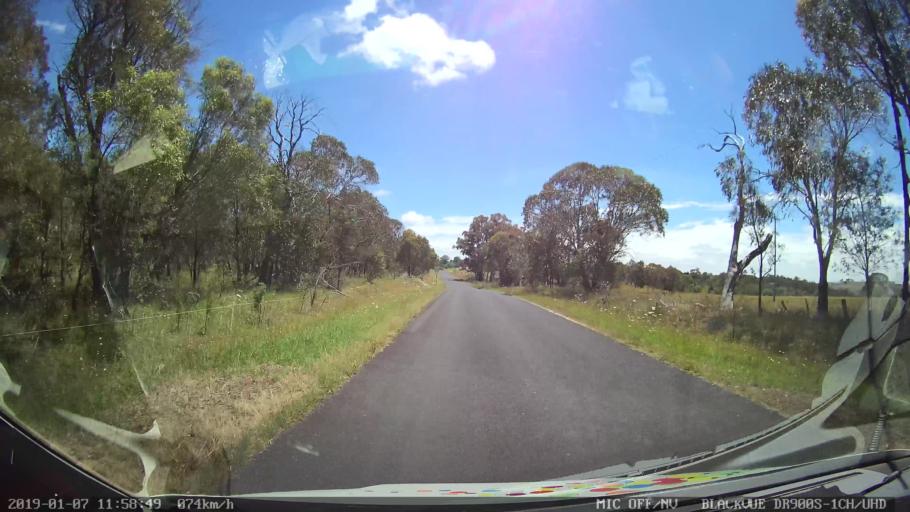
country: AU
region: New South Wales
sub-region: Guyra
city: Guyra
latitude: -30.2490
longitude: 151.6685
